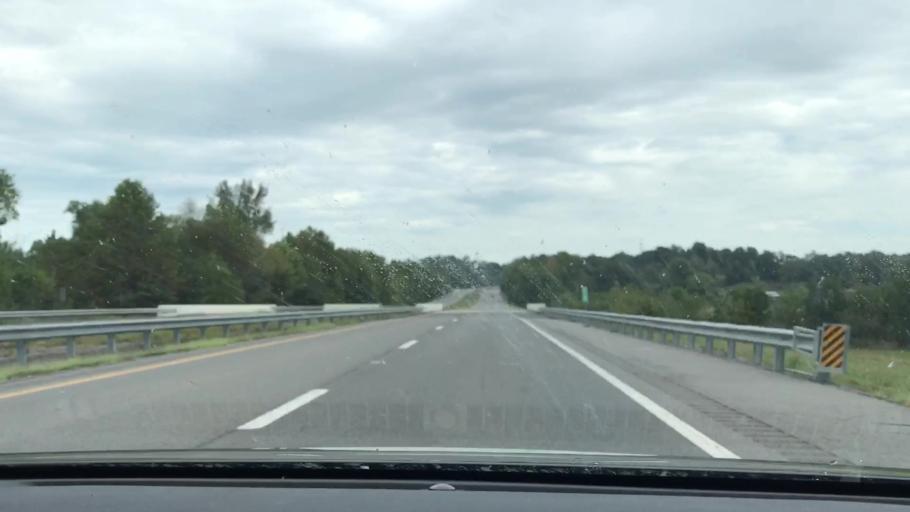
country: US
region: Kentucky
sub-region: Marshall County
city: Benton
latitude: 36.8105
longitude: -88.4903
